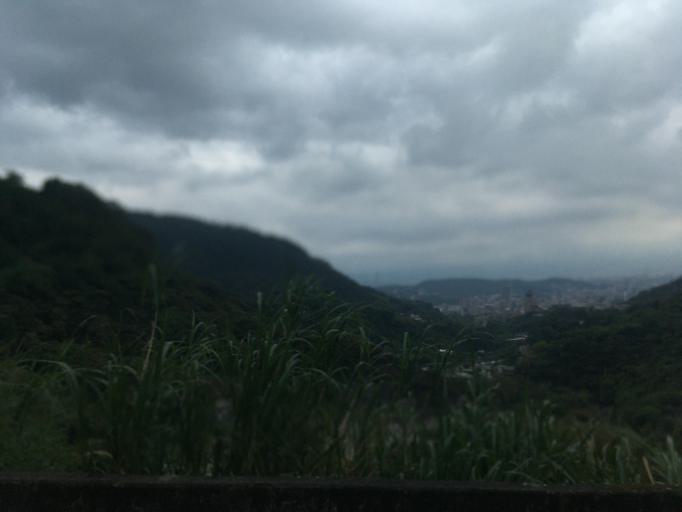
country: TW
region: Taipei
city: Taipei
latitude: 25.1454
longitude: 121.5292
